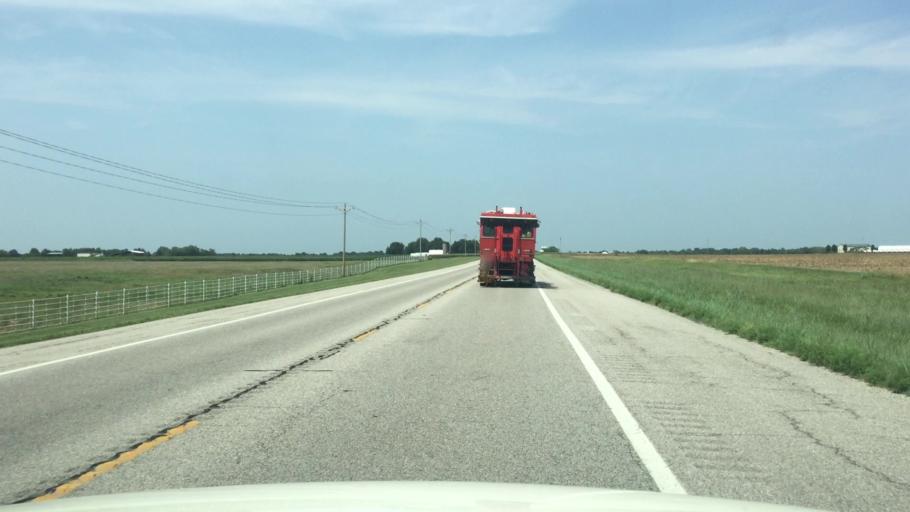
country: US
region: Missouri
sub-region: Jasper County
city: Carl Junction
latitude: 37.2247
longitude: -94.7049
